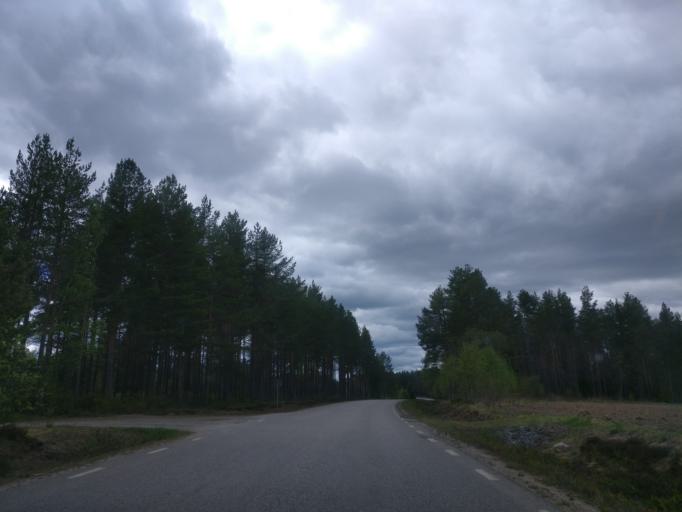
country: SE
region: Gaevleborg
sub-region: Hudiksvalls Kommun
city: Iggesund
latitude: 61.5070
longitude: 17.0133
